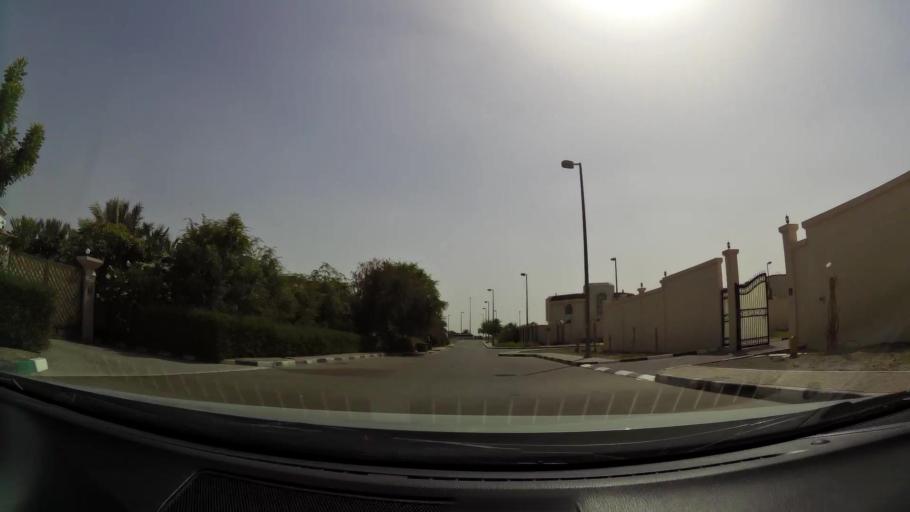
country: AE
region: Abu Dhabi
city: Al Ain
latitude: 24.2308
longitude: 55.6824
